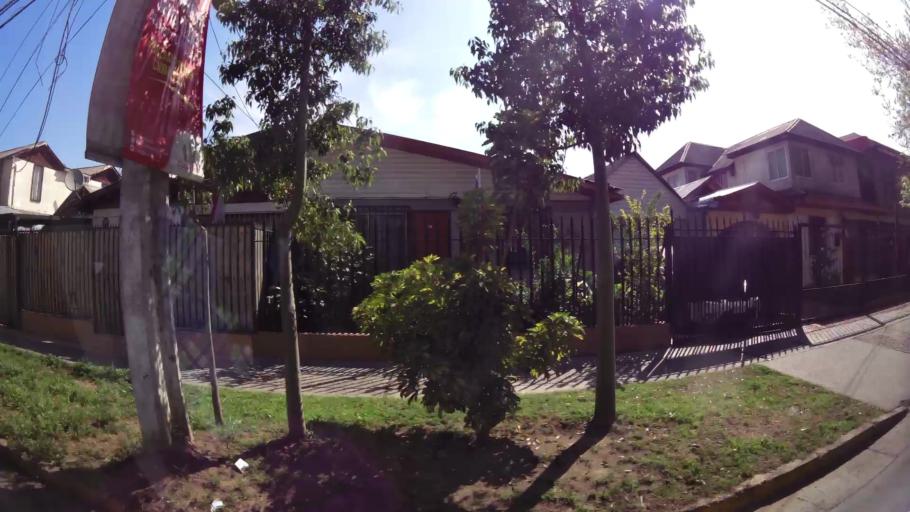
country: CL
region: Santiago Metropolitan
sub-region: Provincia de Santiago
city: Lo Prado
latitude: -33.4789
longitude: -70.7442
